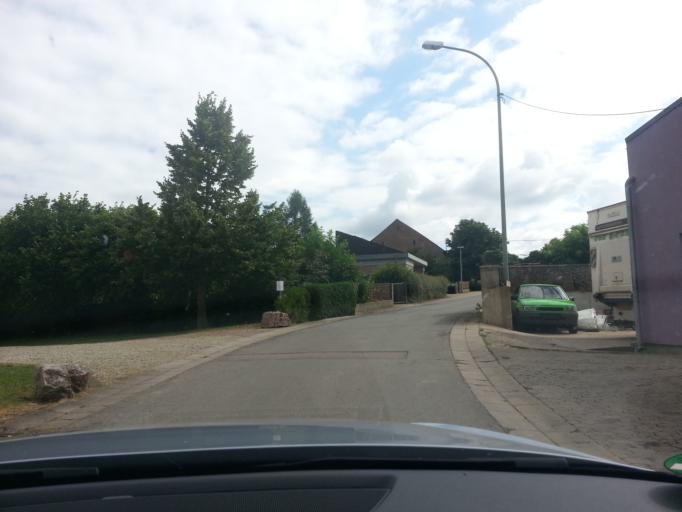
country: DE
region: Rheinland-Pfalz
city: Kirf
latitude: 49.5266
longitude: 6.4871
